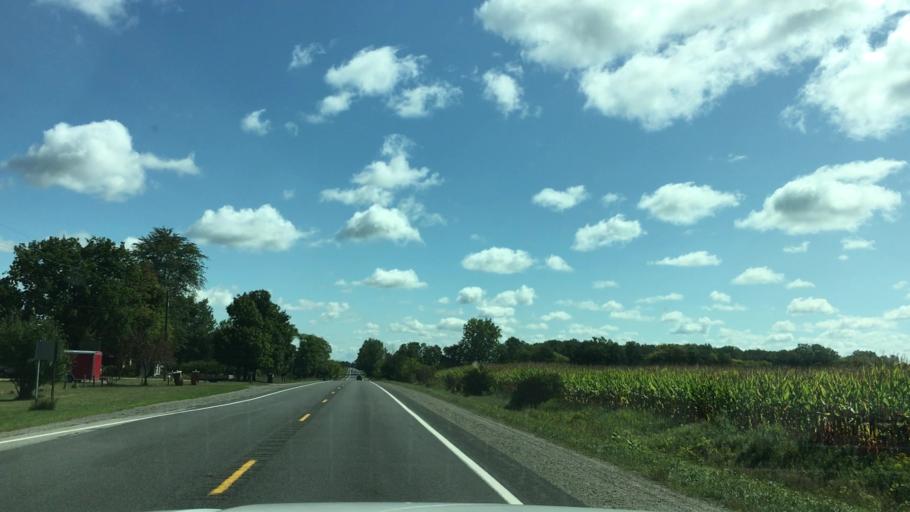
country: US
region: Michigan
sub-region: Montcalm County
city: Carson City
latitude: 43.1774
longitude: -84.9144
